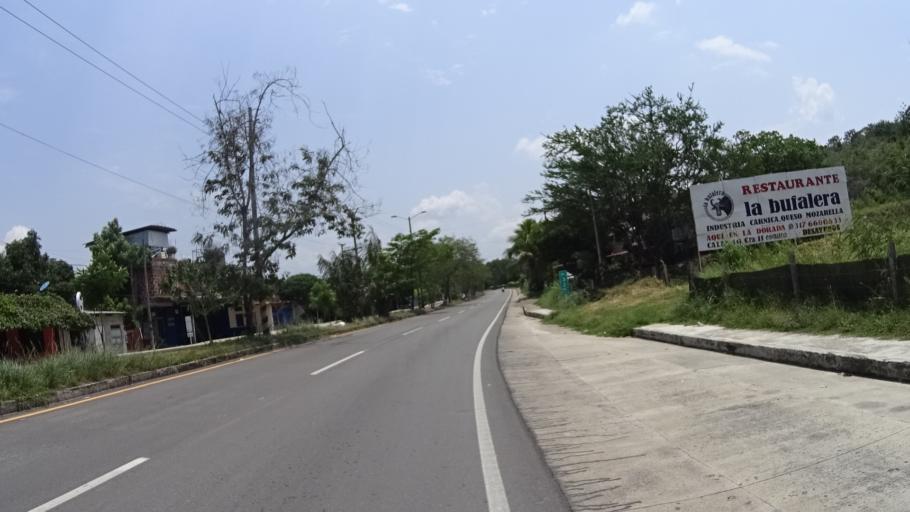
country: CO
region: Caldas
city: La Dorada
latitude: 5.4595
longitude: -74.6704
